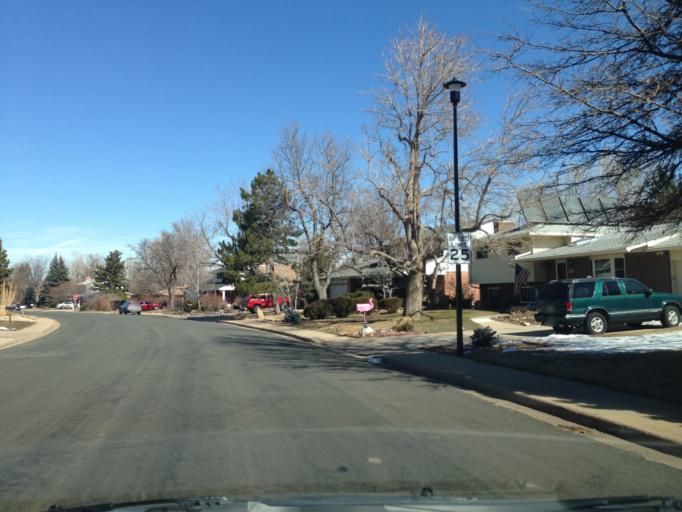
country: US
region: Colorado
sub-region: Boulder County
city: Boulder
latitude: 39.9890
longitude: -105.2275
